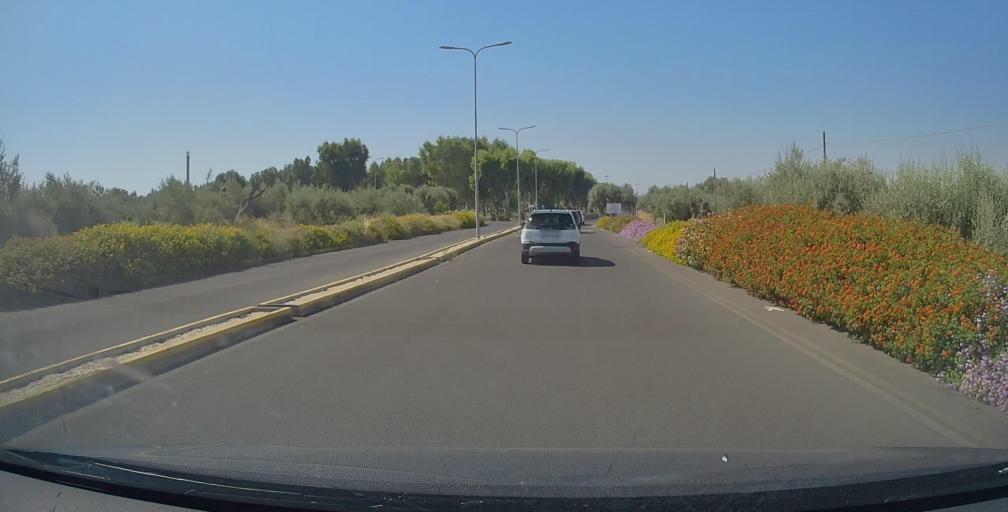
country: IT
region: Sicily
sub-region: Catania
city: Palazzolo
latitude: 37.5397
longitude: 14.9315
